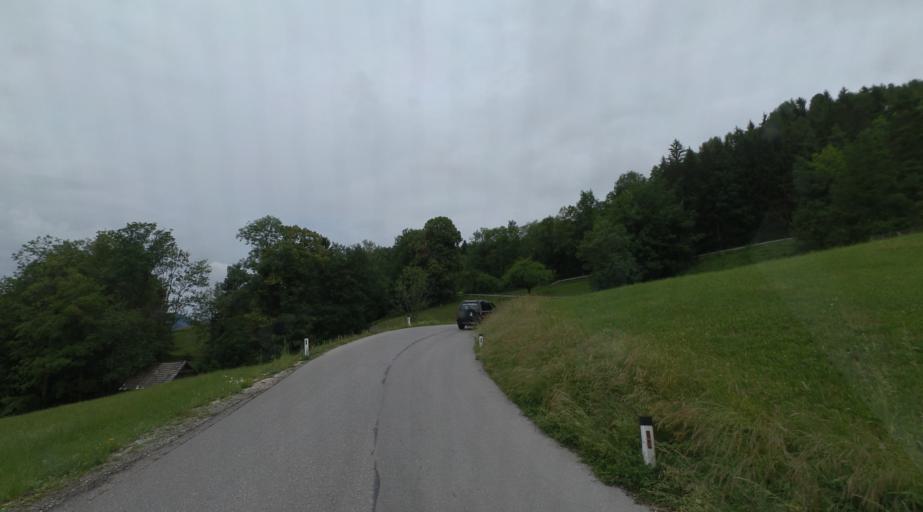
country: AT
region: Upper Austria
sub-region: Politischer Bezirk Kirchdorf an der Krems
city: Micheldorf in Oberoesterreich
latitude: 47.9134
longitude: 14.1455
